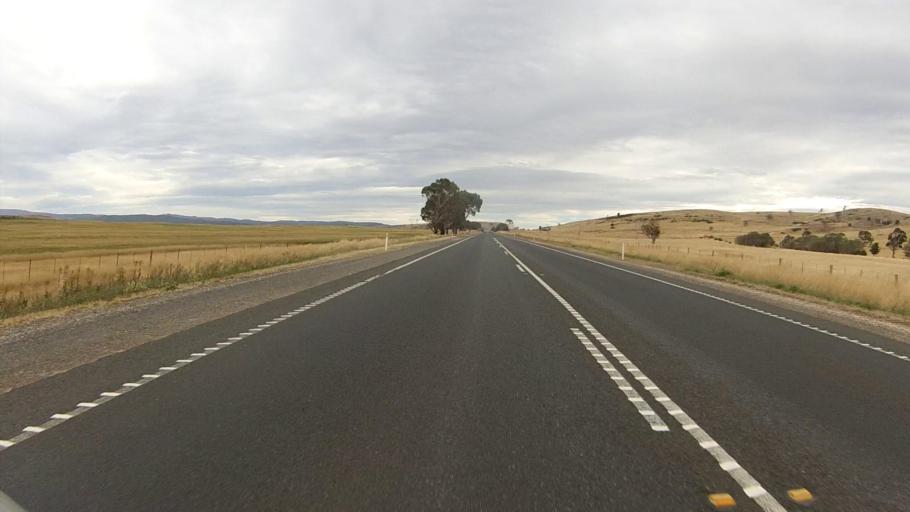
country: AU
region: Tasmania
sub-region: Brighton
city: Bridgewater
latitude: -42.3632
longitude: 147.3359
